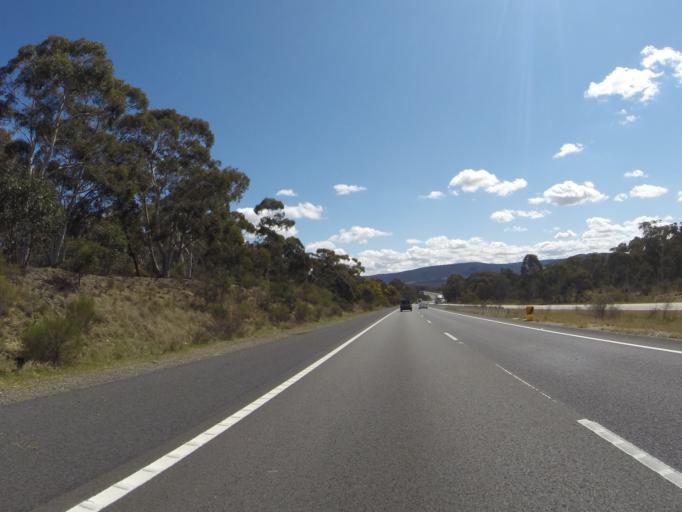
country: AU
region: New South Wales
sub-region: Goulburn Mulwaree
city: Goulburn
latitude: -34.7401
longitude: 149.8366
